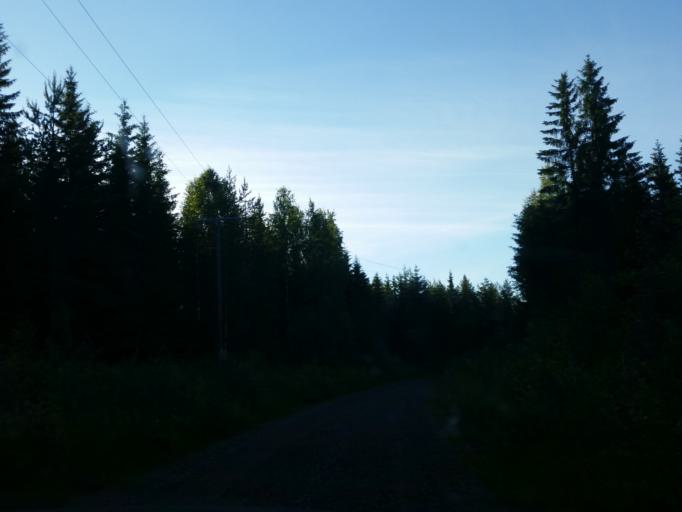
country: FI
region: Northern Savo
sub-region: Sisae-Savo
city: Tervo
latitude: 63.0626
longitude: 26.6116
